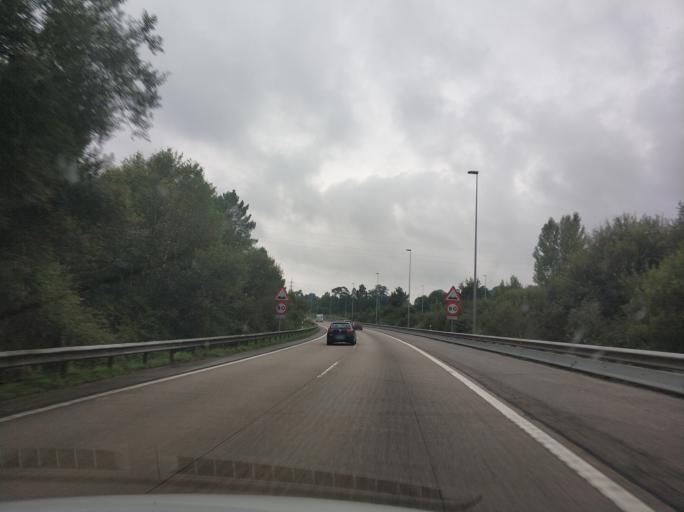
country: ES
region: Asturias
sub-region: Province of Asturias
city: Corvera de Asturias
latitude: 43.5023
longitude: -5.7898
